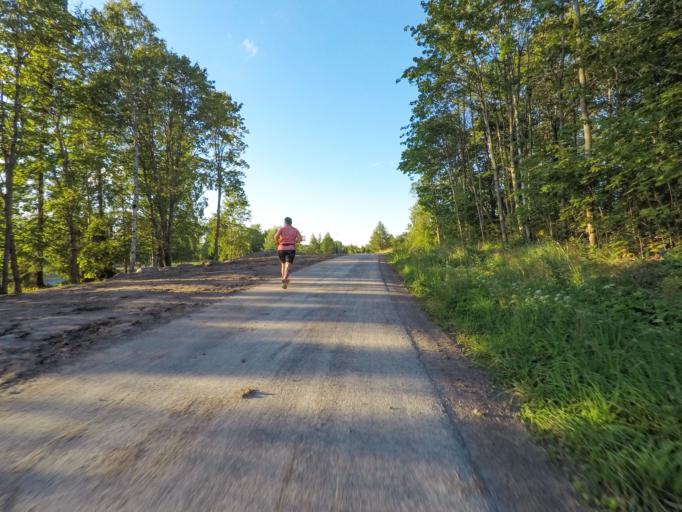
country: FI
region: South Karelia
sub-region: Imatra
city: Imatra
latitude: 61.2000
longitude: 28.7846
